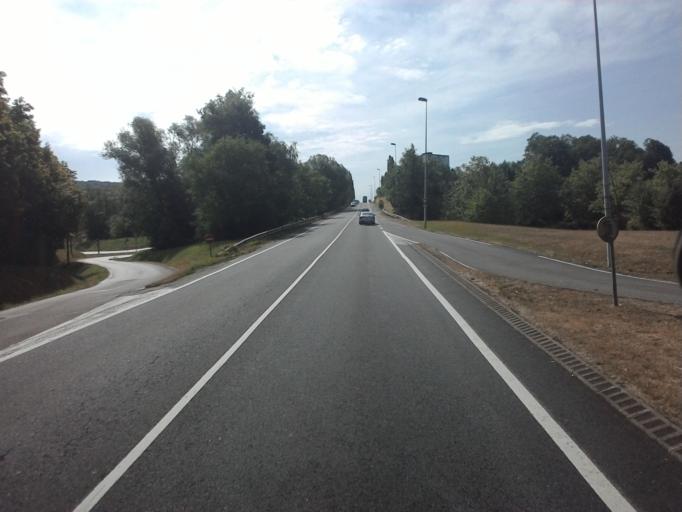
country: FR
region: Franche-Comte
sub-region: Departement du Jura
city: Lons-le-Saunier
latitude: 46.6848
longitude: 5.5668
